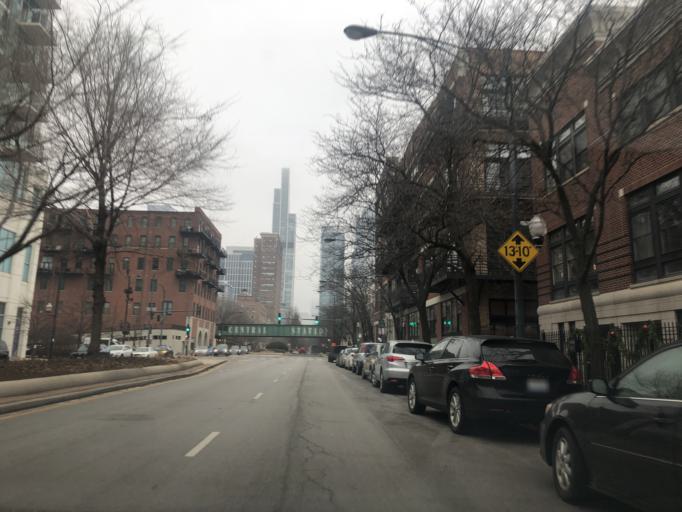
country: US
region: Illinois
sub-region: Cook County
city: Chicago
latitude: 41.8595
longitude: -87.6224
